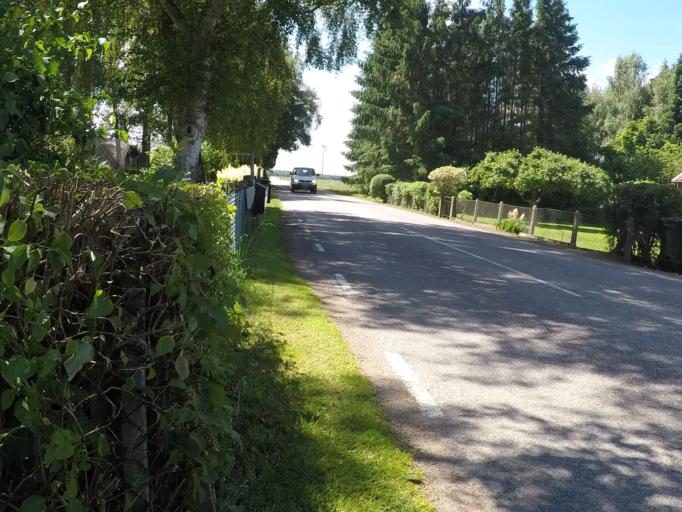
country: SE
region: Skane
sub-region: Malmo
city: Oxie
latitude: 55.5308
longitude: 13.1664
